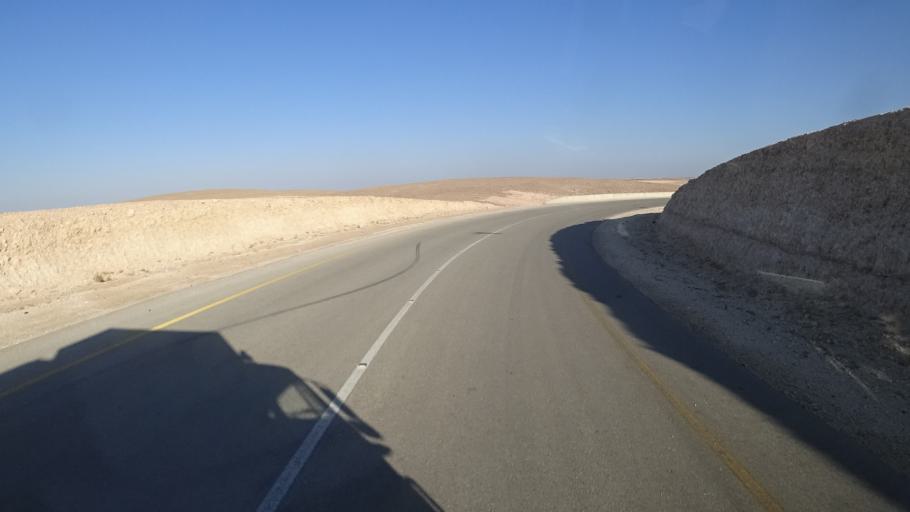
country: YE
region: Al Mahrah
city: Hawf
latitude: 17.0810
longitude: 53.0162
